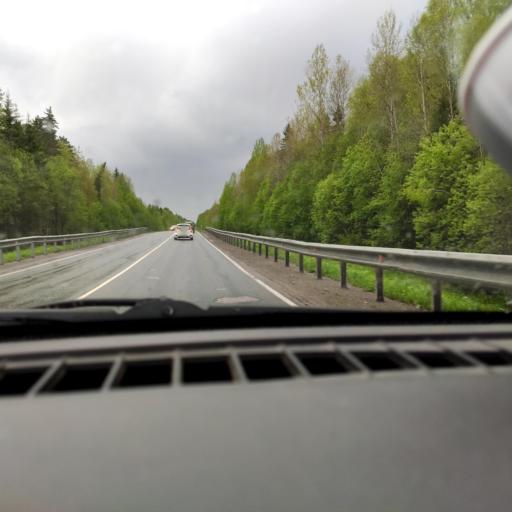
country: RU
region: Perm
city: Perm
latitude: 58.1624
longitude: 56.2438
